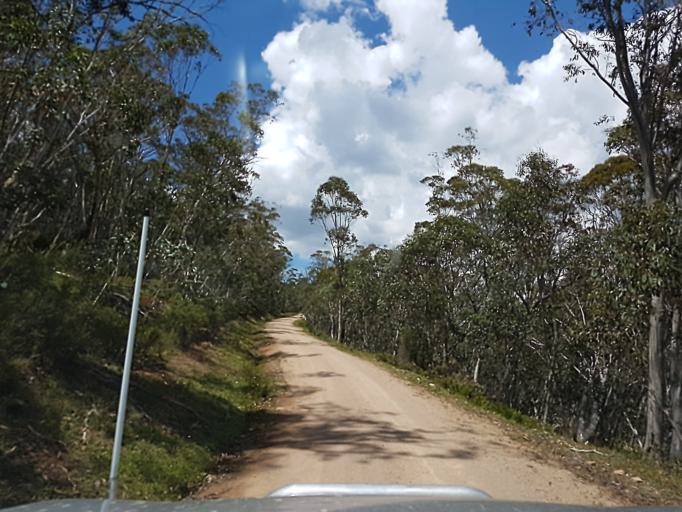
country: AU
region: New South Wales
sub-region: Snowy River
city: Jindabyne
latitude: -36.9240
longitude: 148.1324
